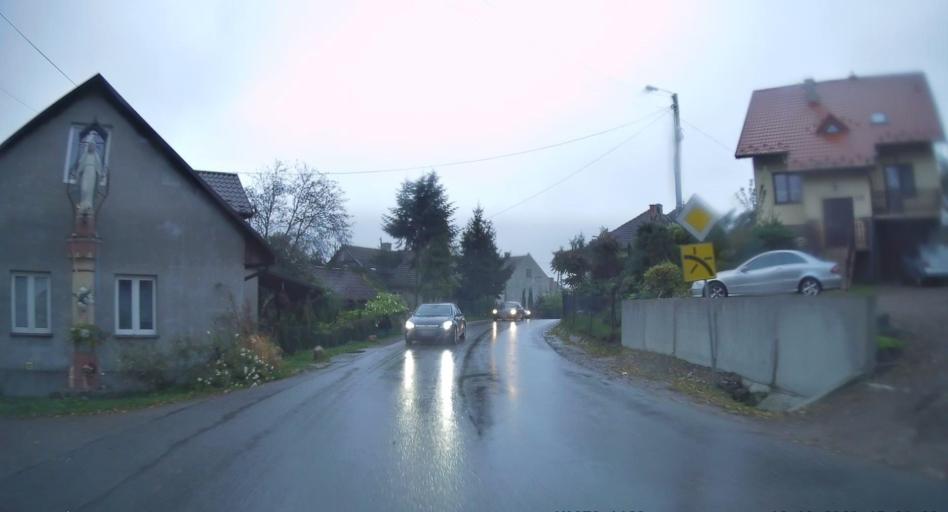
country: PL
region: Lesser Poland Voivodeship
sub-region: Powiat krakowski
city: Ochojno
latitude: 49.9588
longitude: 19.9961
